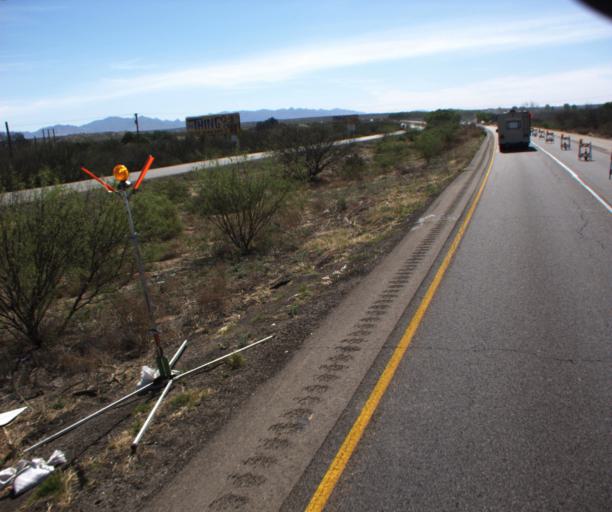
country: US
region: Arizona
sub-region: Cochise County
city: Benson
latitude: 31.9708
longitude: -110.2830
